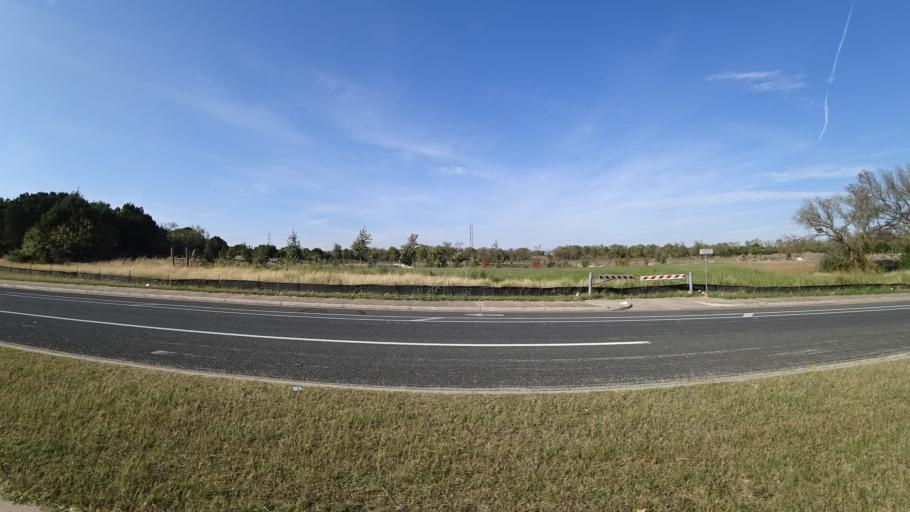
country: US
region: Texas
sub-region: Travis County
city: Wells Branch
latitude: 30.4047
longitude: -97.6546
